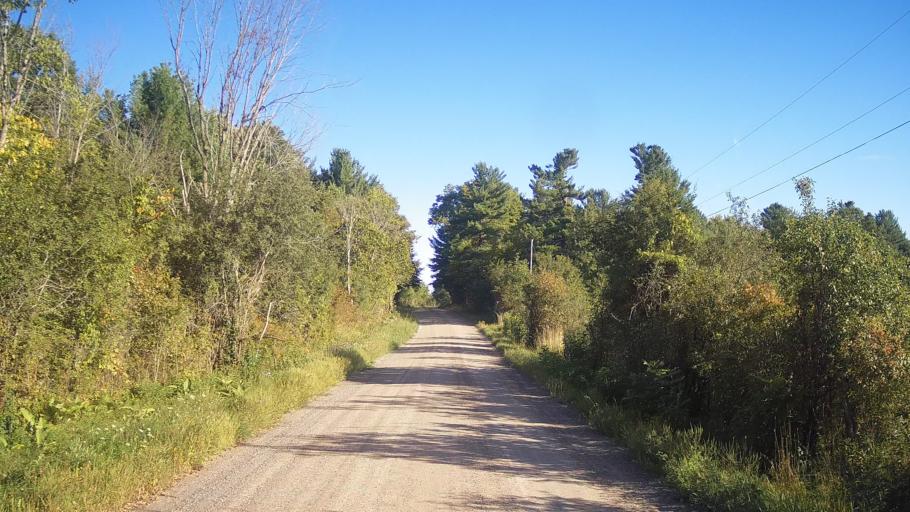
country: US
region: New York
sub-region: Jefferson County
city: Alexandria Bay
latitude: 44.4131
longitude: -75.9767
